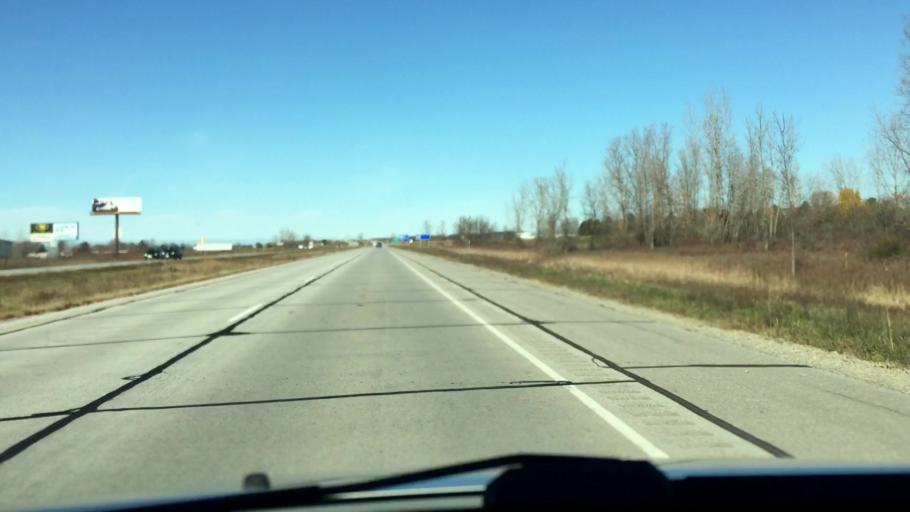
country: US
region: Wisconsin
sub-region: Brown County
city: Pulaski
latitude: 44.5914
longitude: -88.2057
